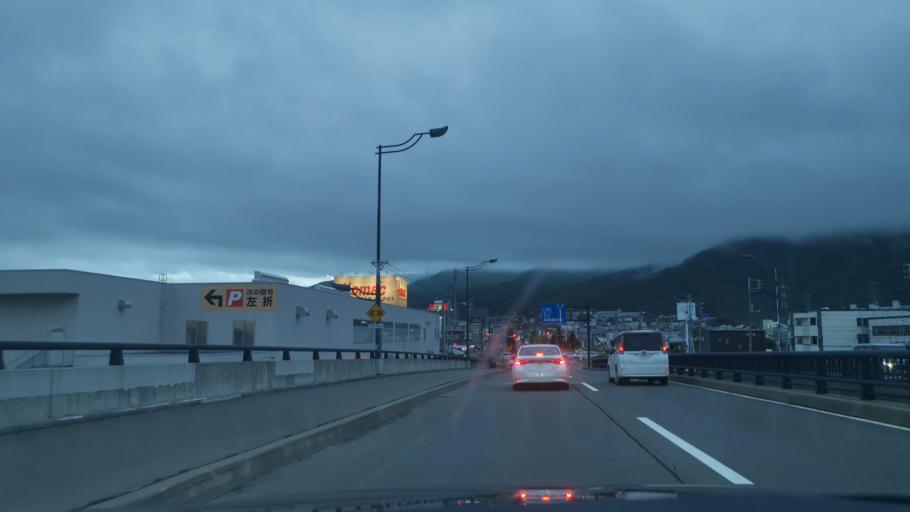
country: JP
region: Hokkaido
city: Sapporo
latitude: 43.1031
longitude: 141.2712
